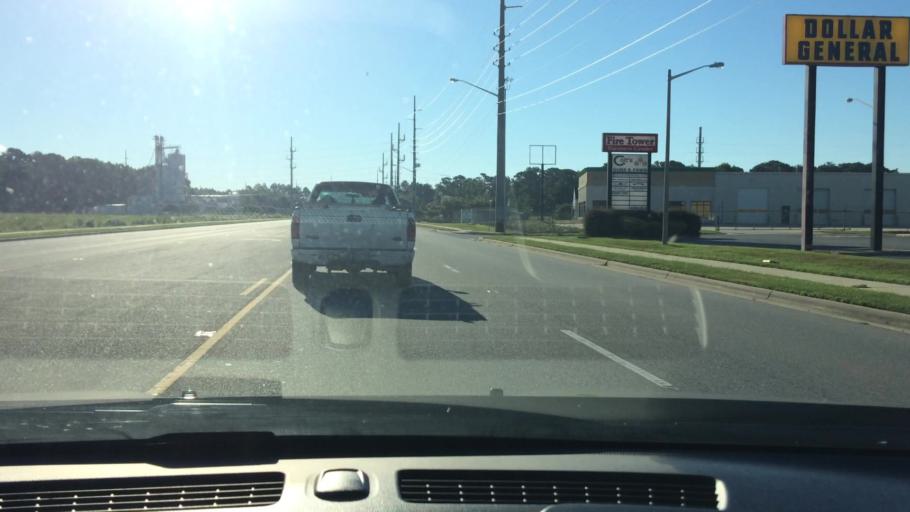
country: US
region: North Carolina
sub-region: Pitt County
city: Winterville
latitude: 35.5480
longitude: -77.3975
